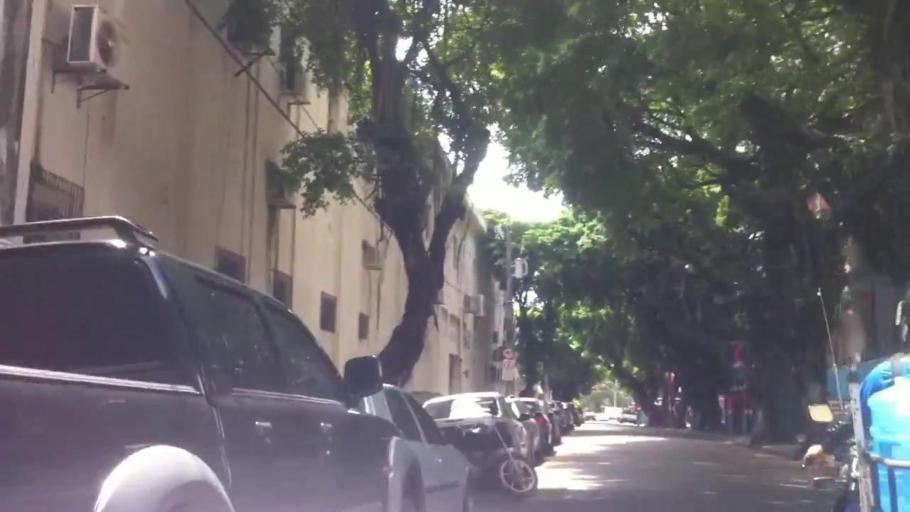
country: BR
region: Pernambuco
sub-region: Recife
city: Recife
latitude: -8.0588
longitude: -34.8847
